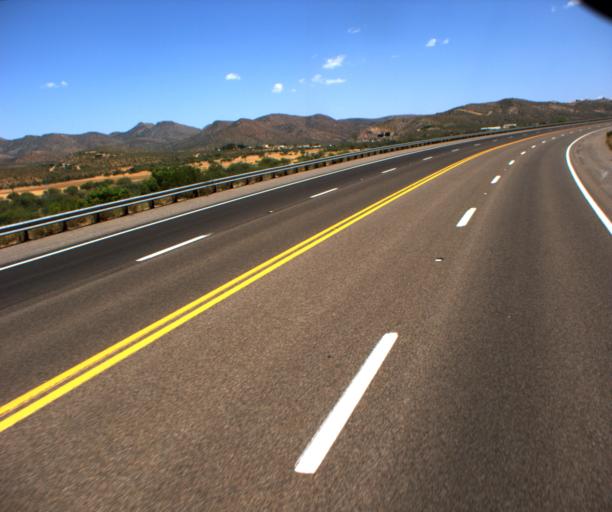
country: US
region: Arizona
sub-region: Gila County
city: Claypool
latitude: 33.4584
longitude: -110.8457
